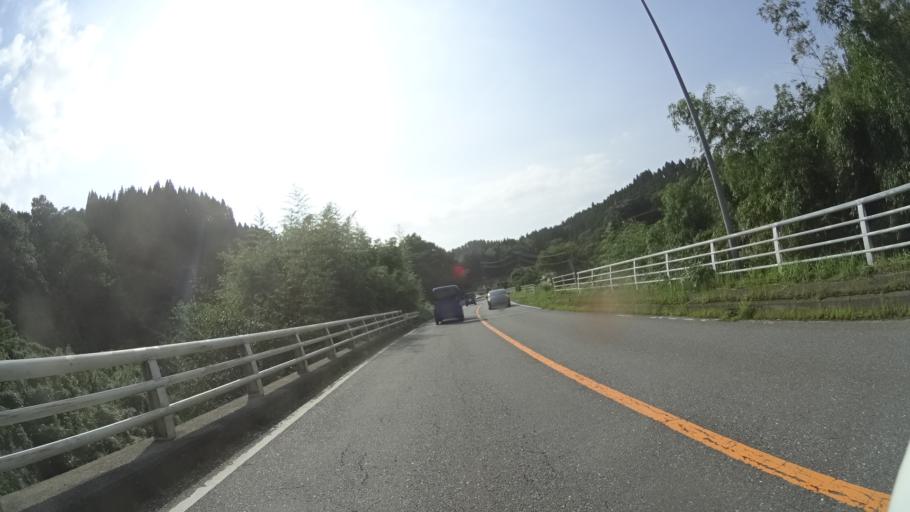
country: JP
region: Kumamoto
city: Aso
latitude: 32.6878
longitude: 131.0721
